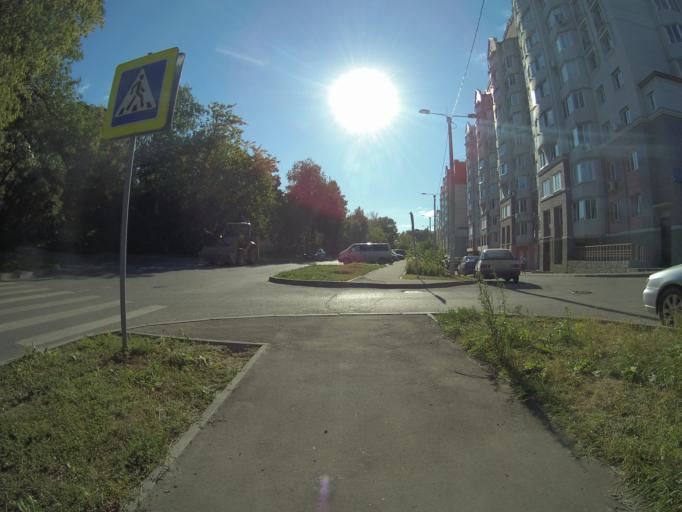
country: RU
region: Vladimir
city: Vladimir
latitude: 56.1437
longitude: 40.3957
